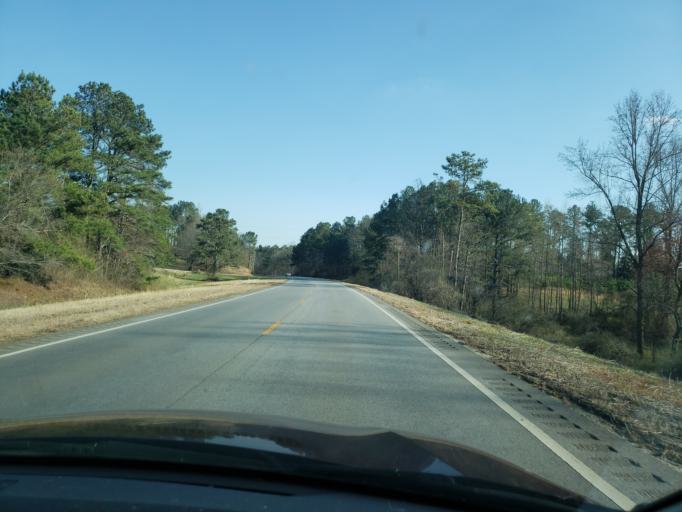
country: US
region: Alabama
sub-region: Randolph County
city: Wedowee
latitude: 33.4134
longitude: -85.5462
